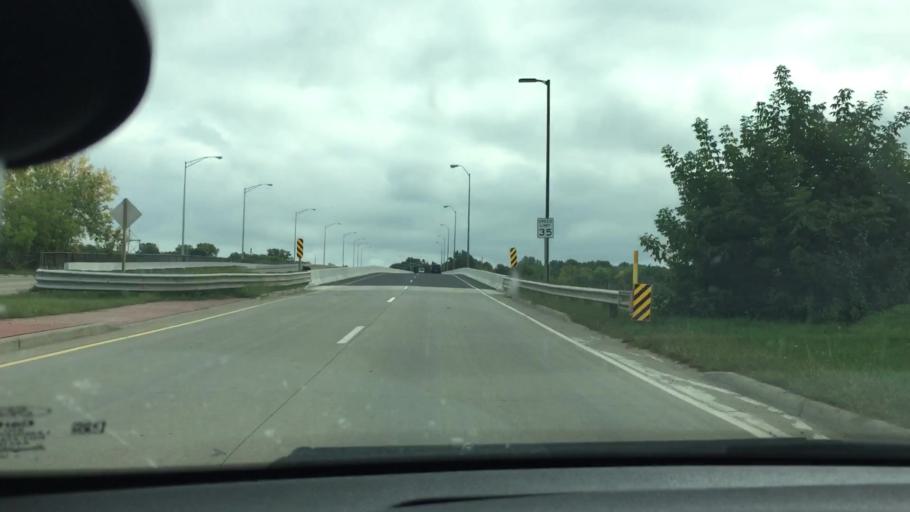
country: US
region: Wisconsin
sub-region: Chippewa County
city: Chippewa Falls
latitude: 44.9326
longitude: -91.3883
